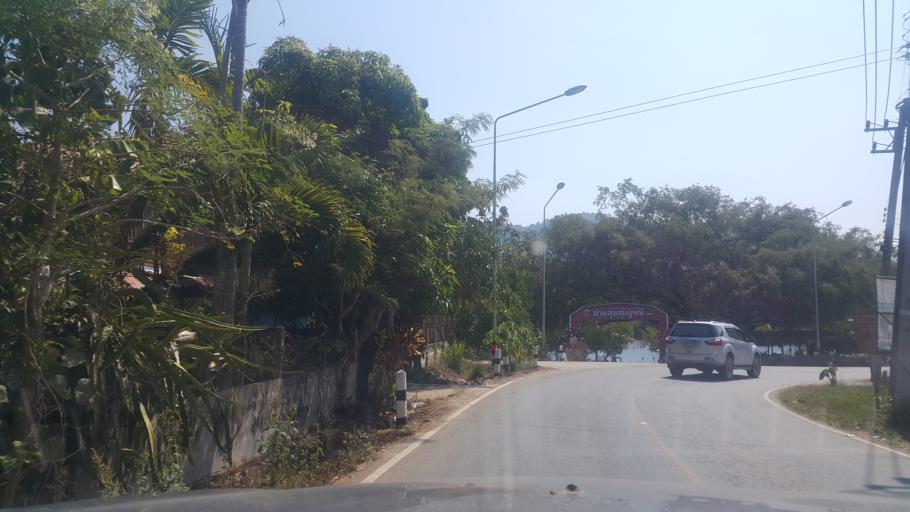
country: TH
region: Nakhon Ratchasima
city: Wang Nam Khiao
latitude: 14.3465
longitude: 101.9416
